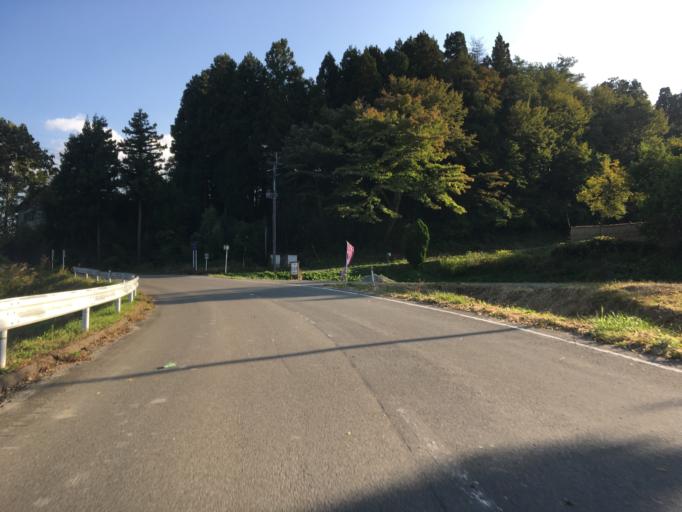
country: JP
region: Fukushima
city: Nihommatsu
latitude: 37.6315
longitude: 140.5568
